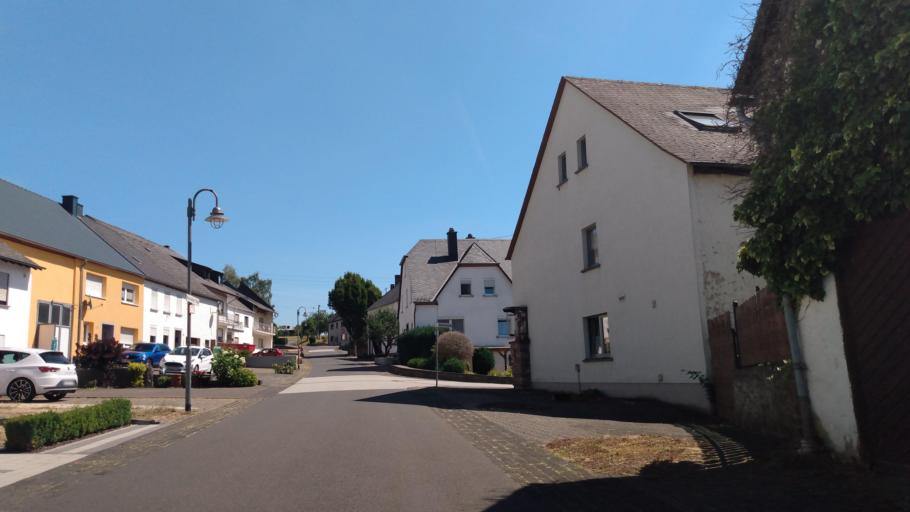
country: DE
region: Rheinland-Pfalz
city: Gornhausen
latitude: 49.8238
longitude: 7.0668
